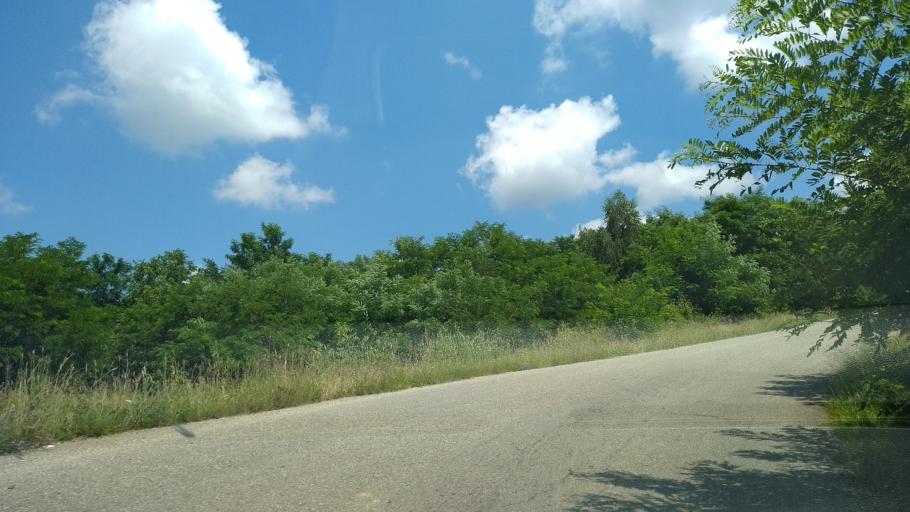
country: RO
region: Hunedoara
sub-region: Comuna Orastioara de Sus
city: Orastioara de Sus
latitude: 45.7075
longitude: 23.1411
